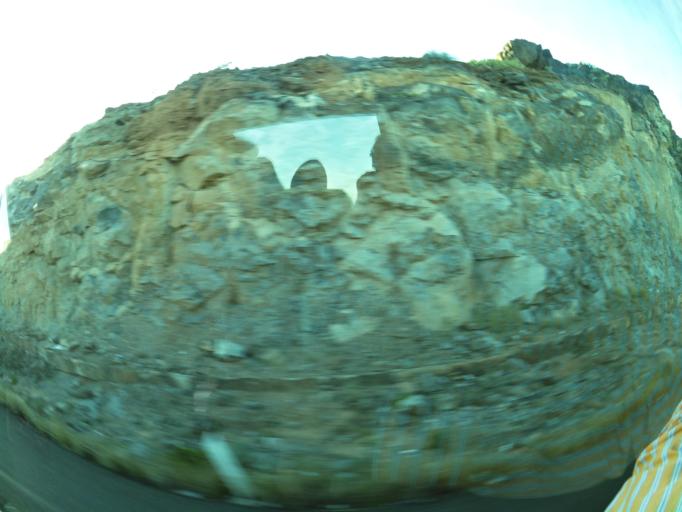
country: ES
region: Canary Islands
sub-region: Provincia de Las Palmas
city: Playa del Ingles
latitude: 27.7741
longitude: -15.5334
